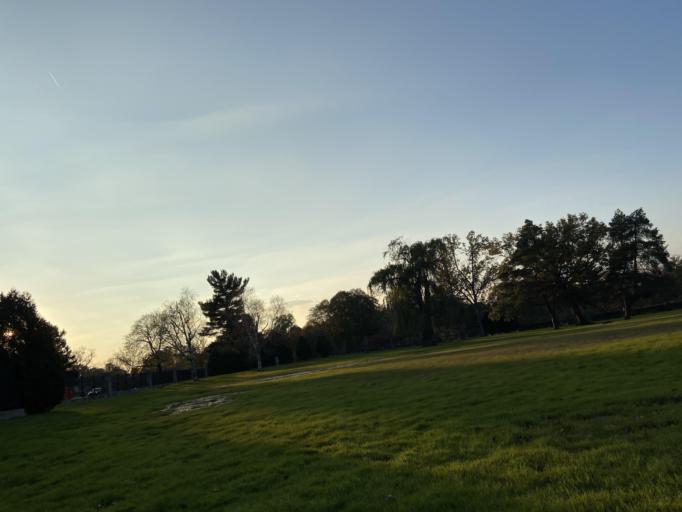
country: US
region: Michigan
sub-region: Wayne County
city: Redford
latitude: 42.4131
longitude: -83.3270
